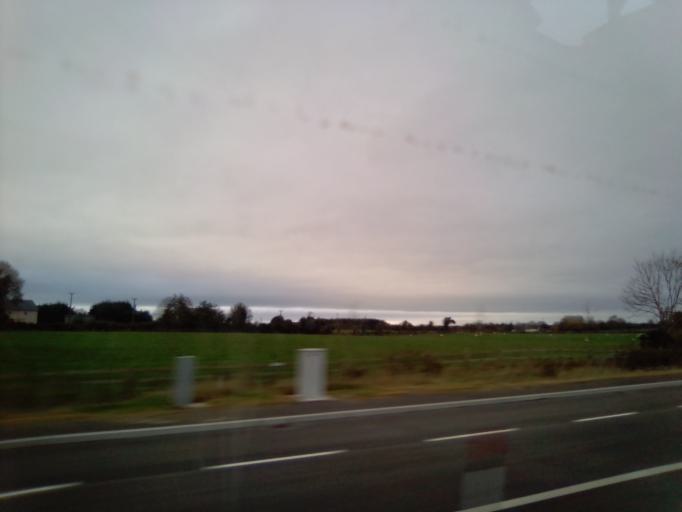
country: IE
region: Connaught
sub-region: County Galway
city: Oranmore
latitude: 53.1918
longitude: -8.8315
